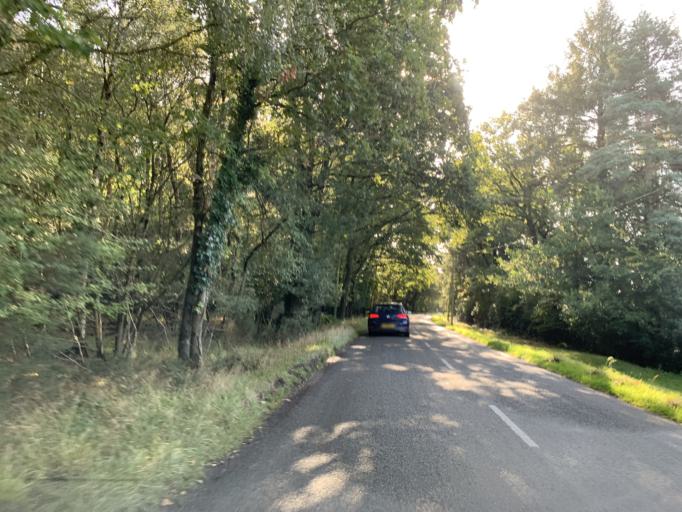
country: GB
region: England
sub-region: Wiltshire
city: Downton
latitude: 50.9708
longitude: -1.7100
